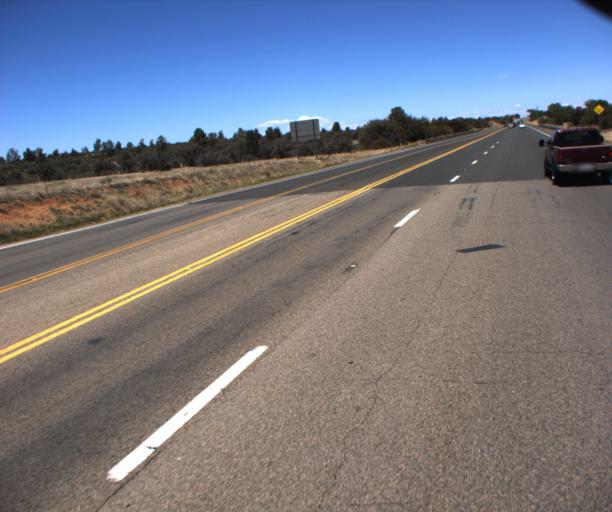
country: US
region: Arizona
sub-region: Yavapai County
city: Prescott
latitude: 34.6335
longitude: -112.4293
